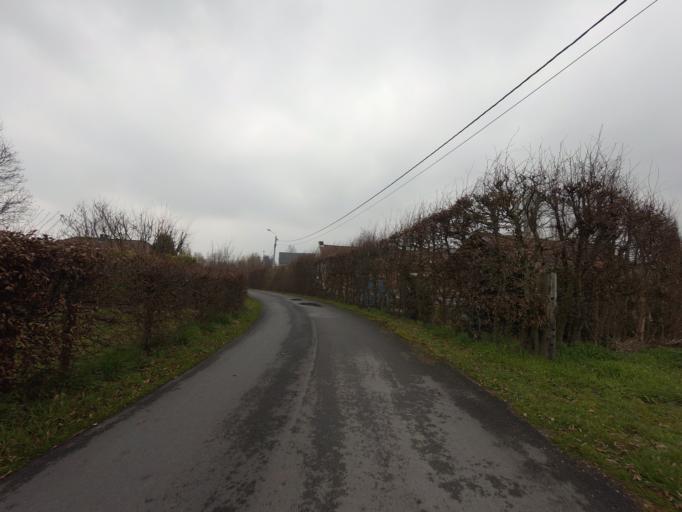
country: BE
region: Flanders
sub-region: Provincie Antwerpen
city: Putte
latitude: 51.0642
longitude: 4.5985
